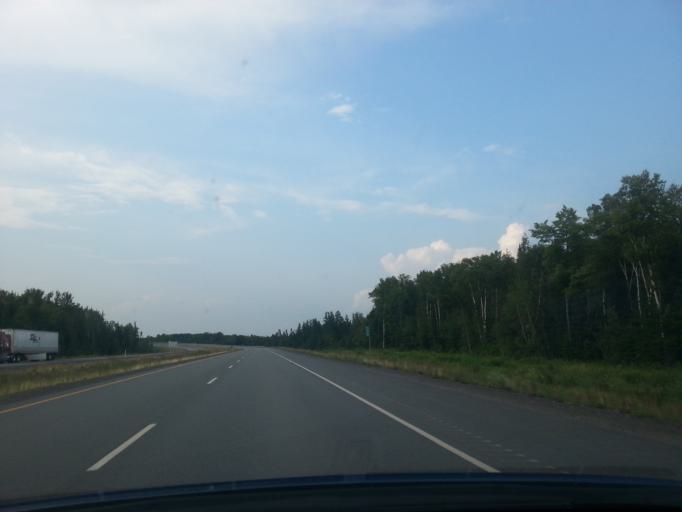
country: CA
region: New Brunswick
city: Harrison Brook
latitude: 47.2035
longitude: -67.9306
